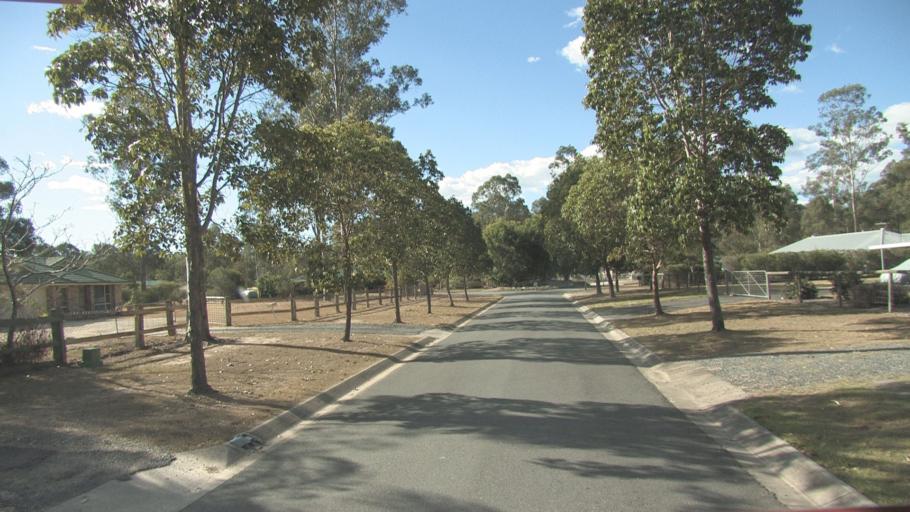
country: AU
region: Queensland
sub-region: Logan
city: North Maclean
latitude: -27.8014
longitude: 152.9701
